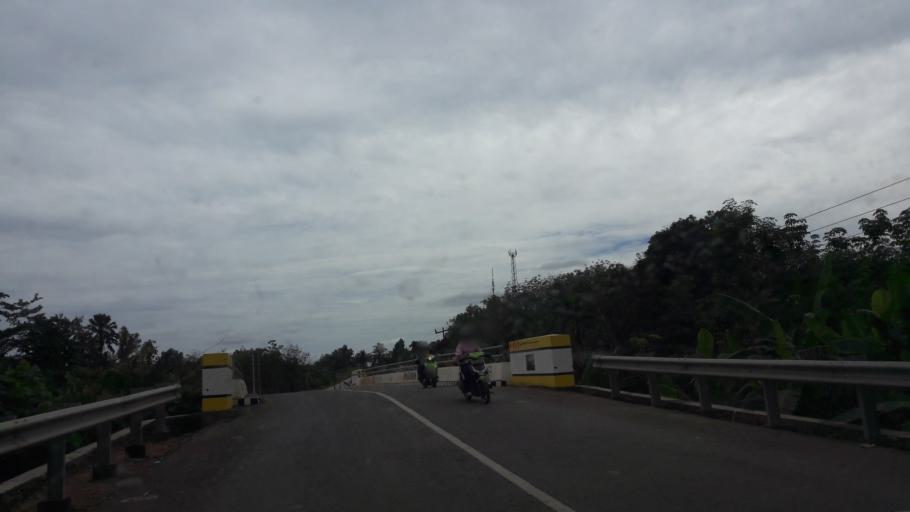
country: ID
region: South Sumatra
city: Gunungmegang Dalam
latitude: -3.2598
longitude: 103.8298
